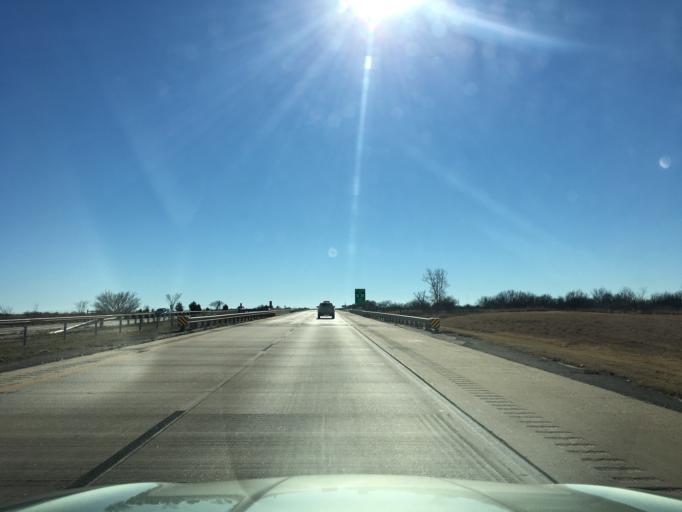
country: US
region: Oklahoma
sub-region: Noble County
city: Perry
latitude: 36.4356
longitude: -97.3271
